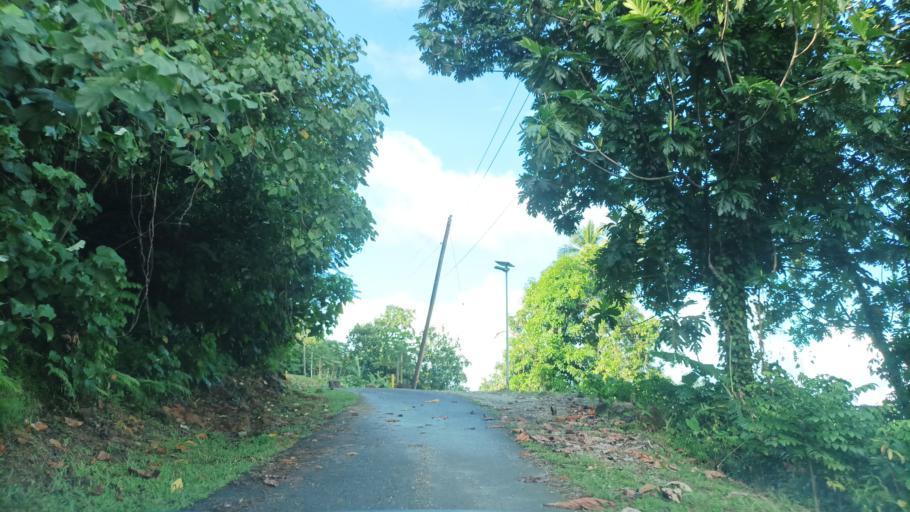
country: FM
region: Pohnpei
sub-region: Kolonia Municipality
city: Kolonia Town
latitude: 6.9647
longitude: 158.1936
